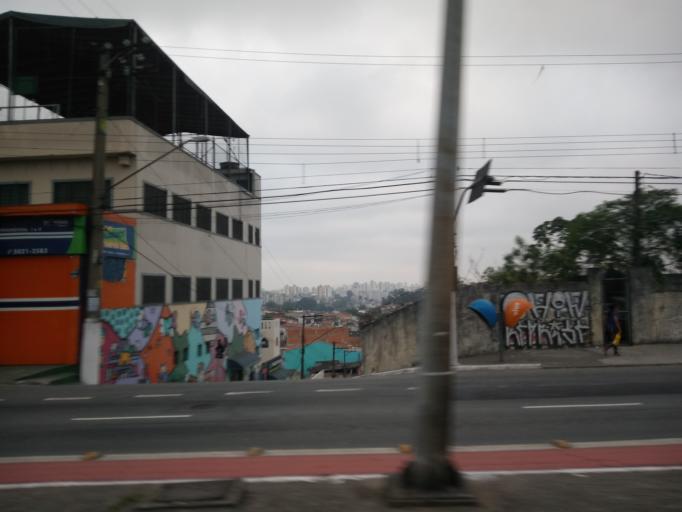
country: BR
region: Sao Paulo
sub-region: Diadema
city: Diadema
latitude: -23.6600
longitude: -46.6367
